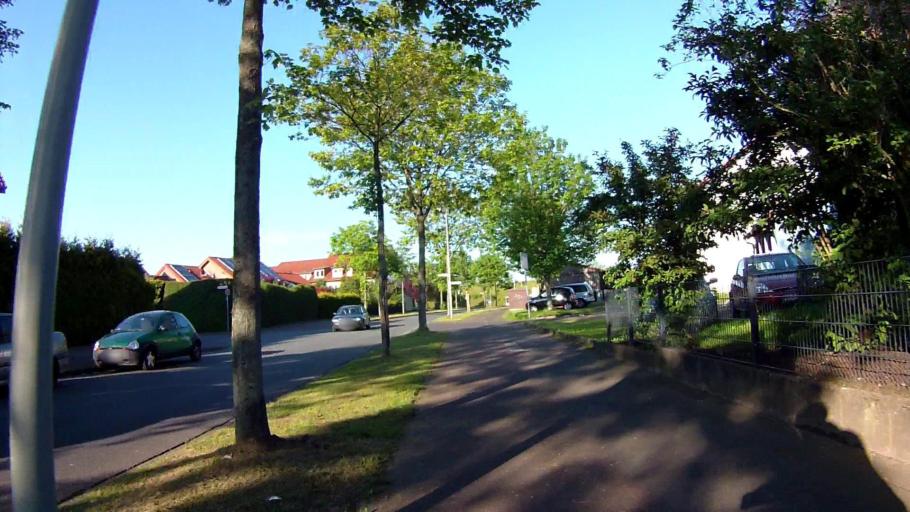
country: DE
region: North Rhine-Westphalia
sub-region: Regierungsbezirk Detmold
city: Paderborn
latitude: 51.7158
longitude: 8.7961
